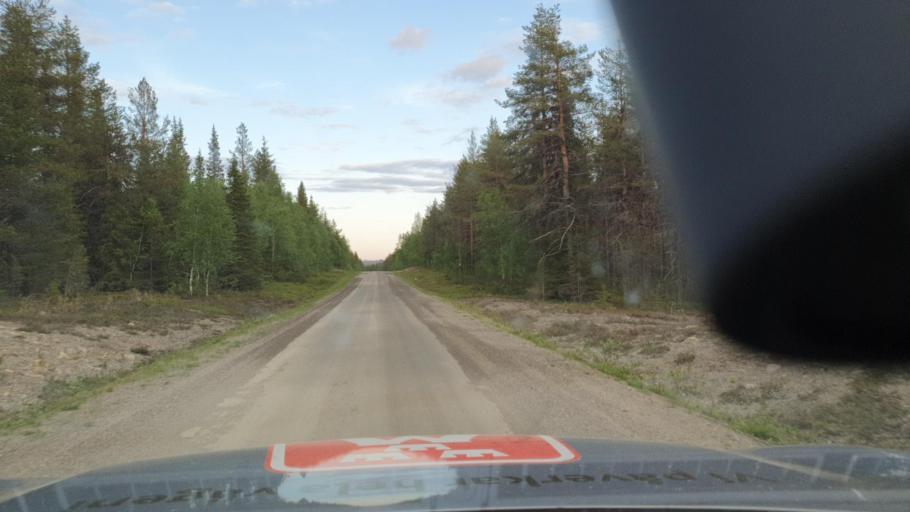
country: SE
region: Norrbotten
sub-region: Bodens Kommun
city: Boden
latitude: 66.5882
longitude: 21.3875
